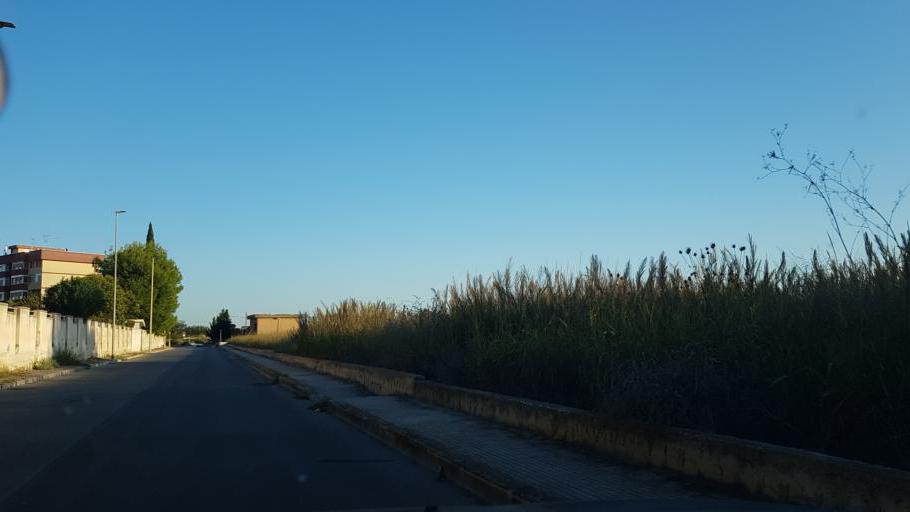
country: IT
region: Apulia
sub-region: Provincia di Brindisi
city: Brindisi
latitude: 40.6187
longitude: 17.9144
